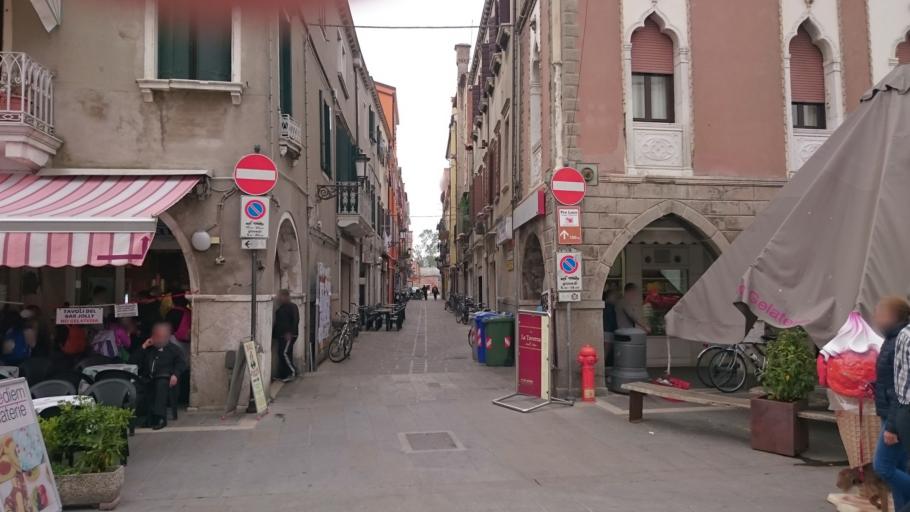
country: IT
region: Veneto
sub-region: Provincia di Venezia
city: Chioggia
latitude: 45.2201
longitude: 12.2791
